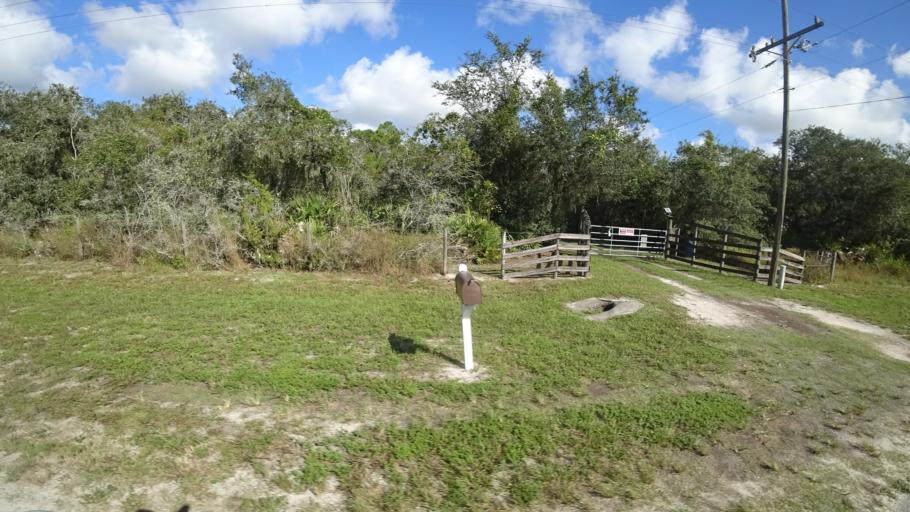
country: US
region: Florida
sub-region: Sarasota County
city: Lake Sarasota
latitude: 27.3392
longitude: -82.1889
